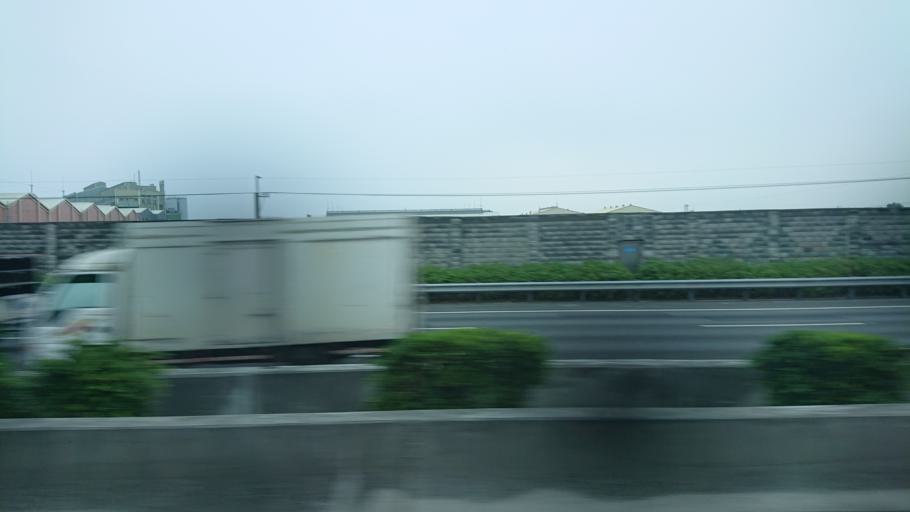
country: TW
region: Taiwan
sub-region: Yunlin
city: Douliu
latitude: 23.8472
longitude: 120.4844
